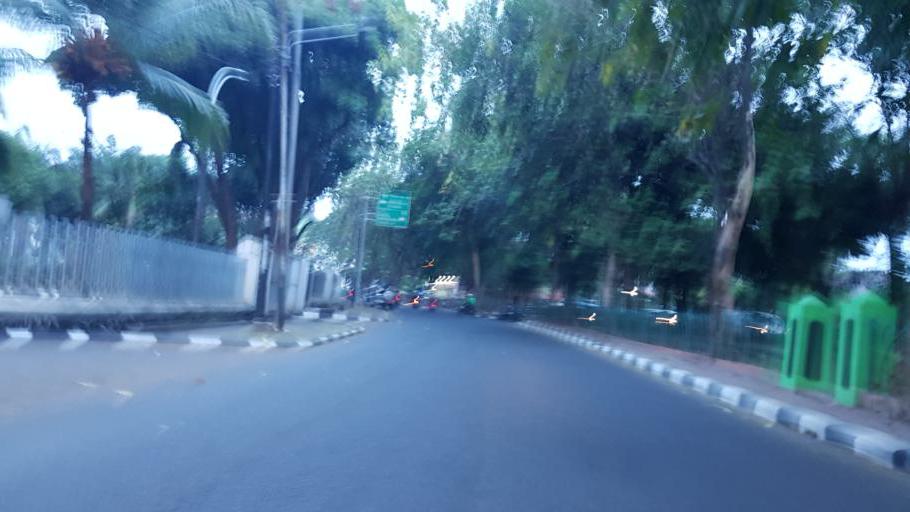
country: ID
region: West Java
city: Pamulang
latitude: -6.3153
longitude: 106.7919
